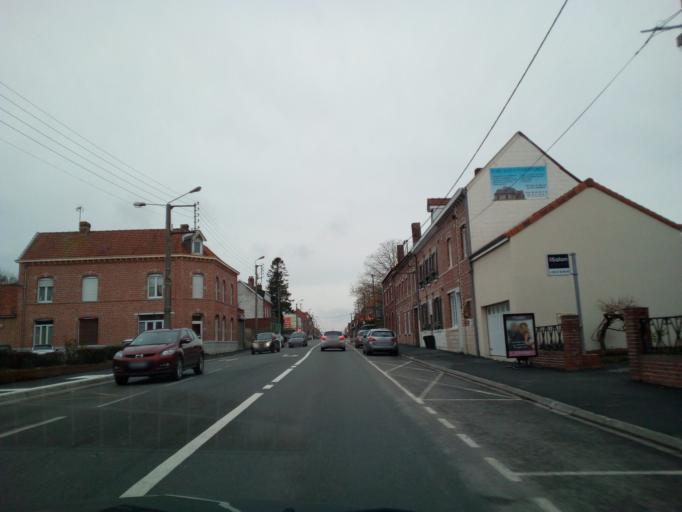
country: FR
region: Nord-Pas-de-Calais
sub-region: Departement du Pas-de-Calais
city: Cuinchy
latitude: 50.5119
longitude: 2.7417
